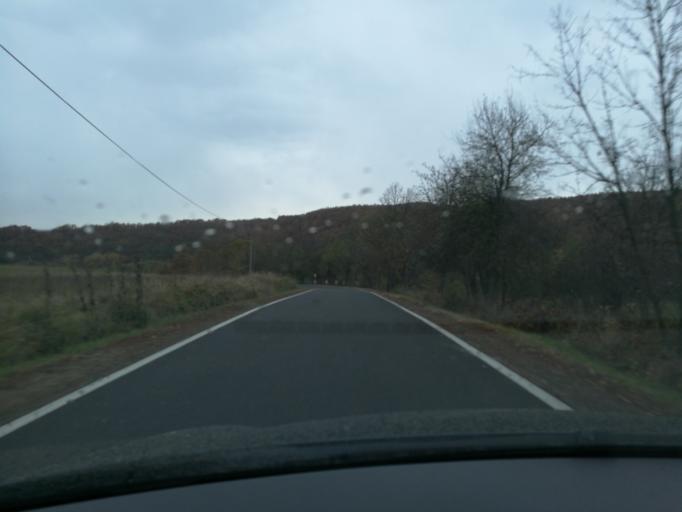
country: HU
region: Nograd
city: Paszto
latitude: 47.9761
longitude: 19.6311
